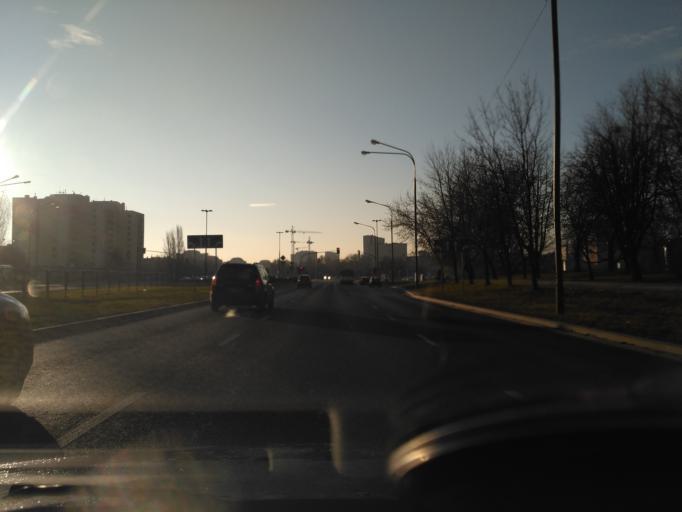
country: PL
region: Lublin Voivodeship
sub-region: Powiat lubelski
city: Lublin
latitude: 51.2640
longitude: 22.5512
